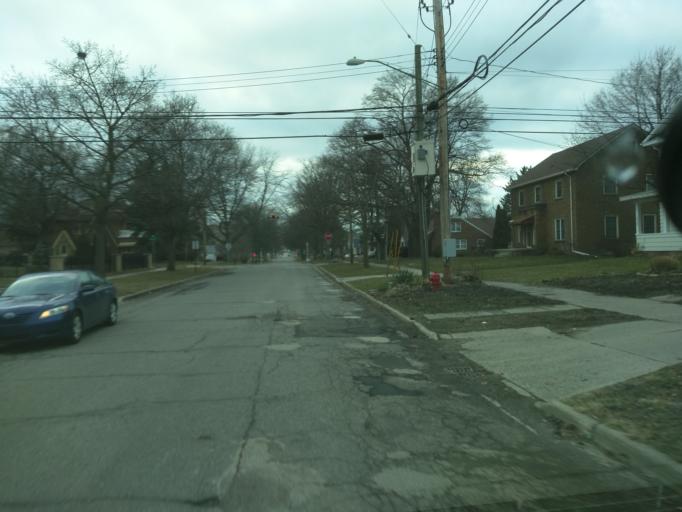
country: US
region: Michigan
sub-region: Ingham County
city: Lansing
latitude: 42.7337
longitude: -84.5720
